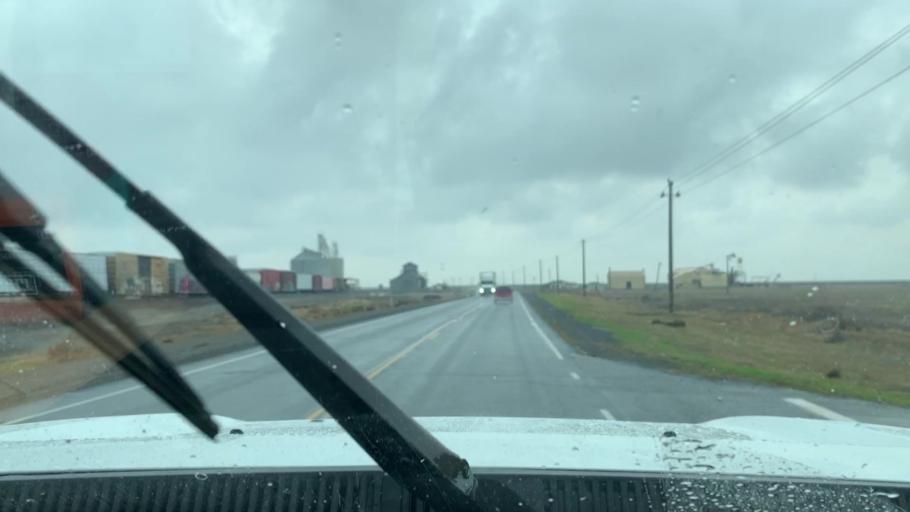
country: US
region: California
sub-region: Tulare County
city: Alpaugh
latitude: 35.9857
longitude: -119.4740
